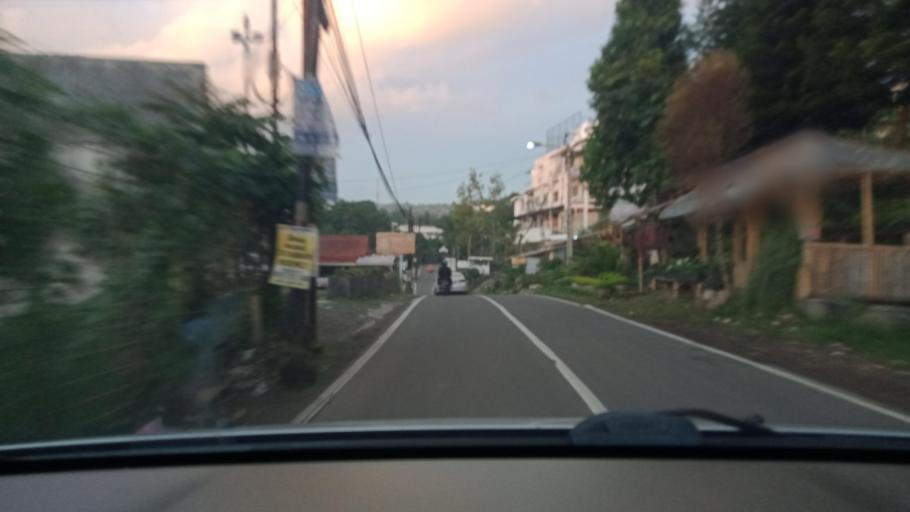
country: ID
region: West Java
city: Lembang
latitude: -6.8501
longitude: 107.5907
